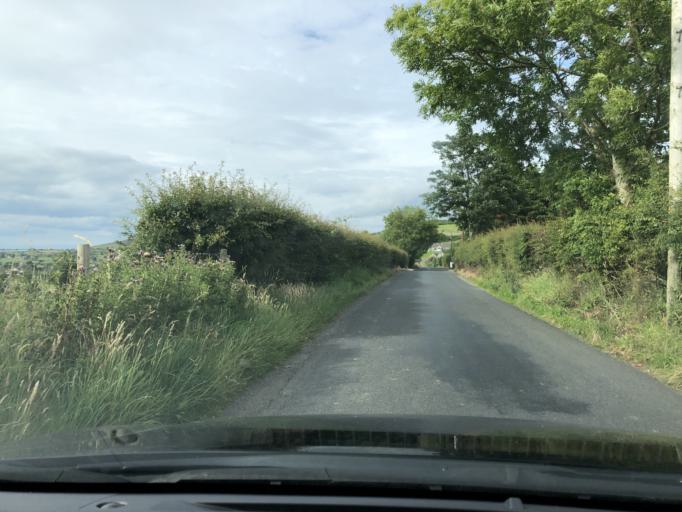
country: GB
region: Northern Ireland
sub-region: Down District
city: Castlewellan
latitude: 54.2273
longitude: -6.0134
